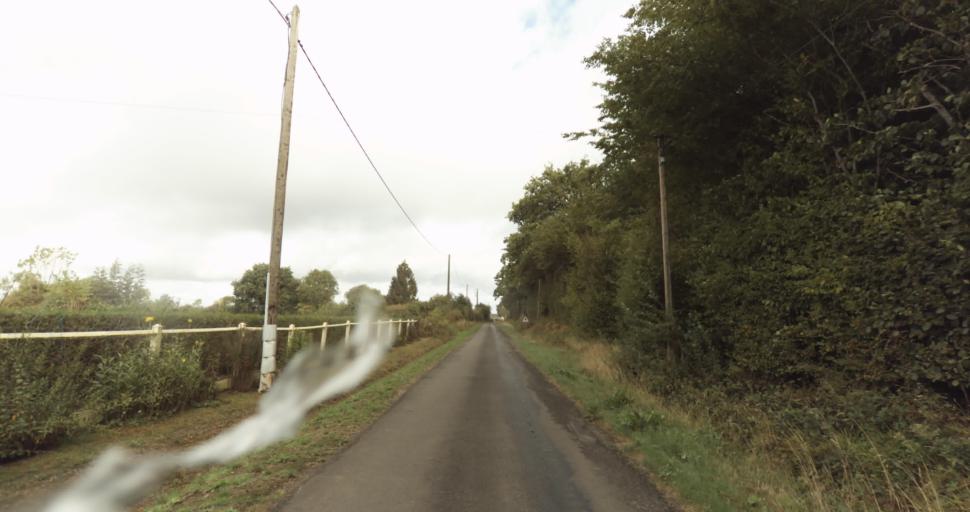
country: FR
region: Lower Normandy
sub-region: Departement de l'Orne
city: Gace
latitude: 48.8463
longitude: 0.3228
